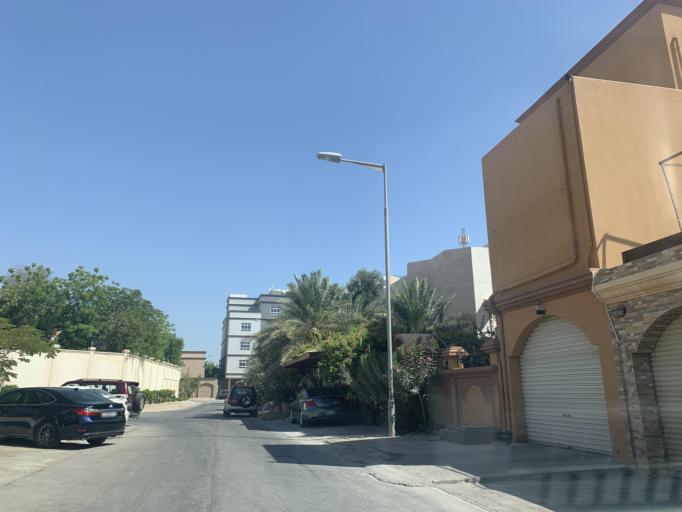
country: BH
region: Manama
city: Jidd Hafs
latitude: 26.2247
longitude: 50.5277
